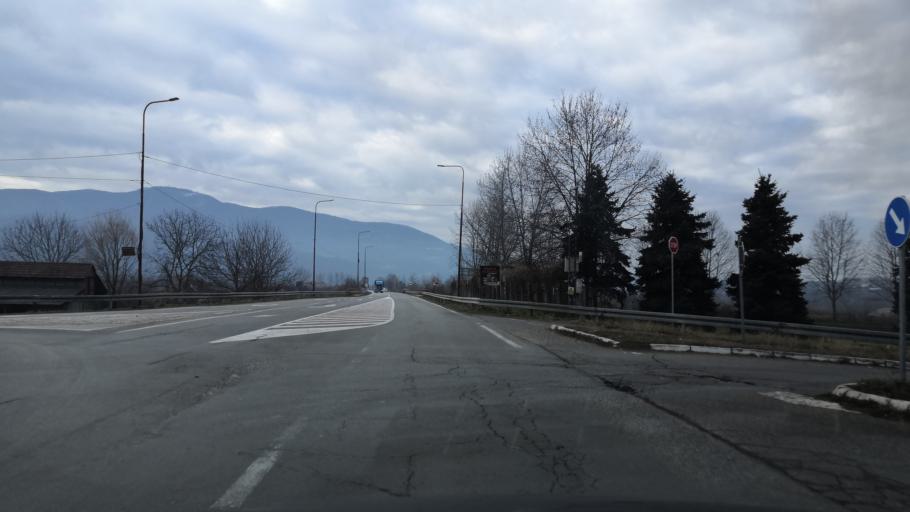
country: RS
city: Trsic
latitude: 44.5362
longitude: 19.1829
